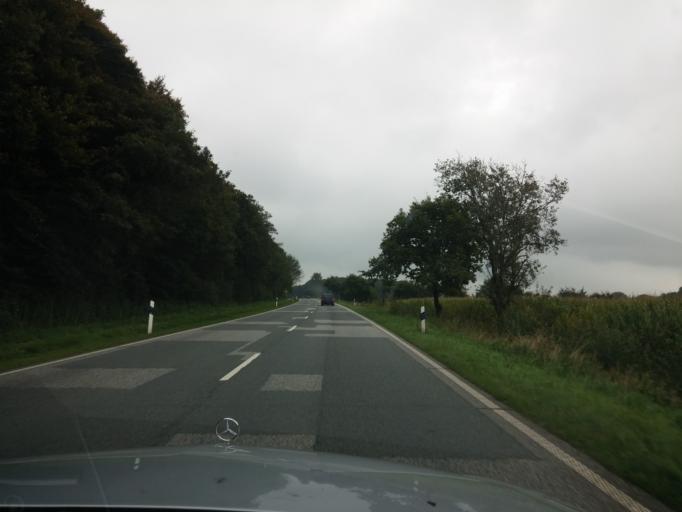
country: DE
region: Schleswig-Holstein
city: Oster-Ohrstedt
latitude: 54.5119
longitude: 9.2668
